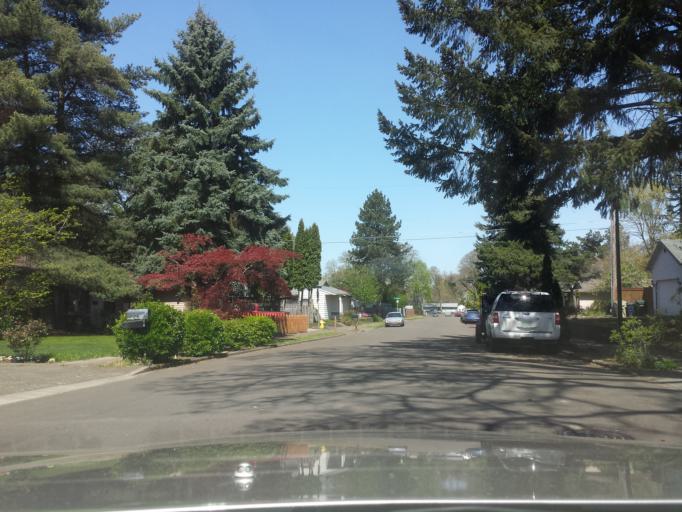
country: US
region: Oregon
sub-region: Washington County
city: Aloha
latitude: 45.4861
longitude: -122.8595
